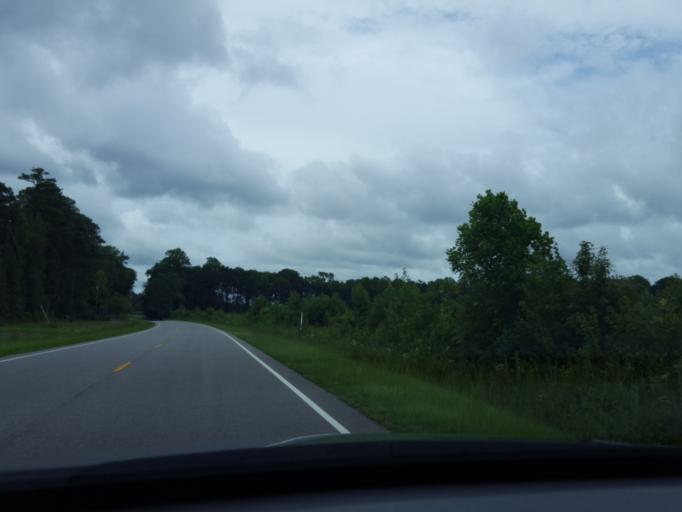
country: US
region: North Carolina
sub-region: Martin County
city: Williamston
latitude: 35.7660
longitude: -76.9557
